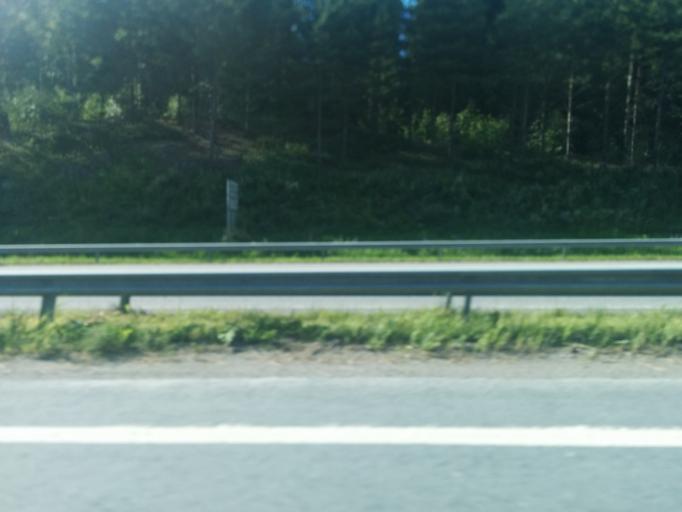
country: FI
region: Pirkanmaa
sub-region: Tampere
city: Tampere
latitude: 61.5050
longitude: 23.8989
